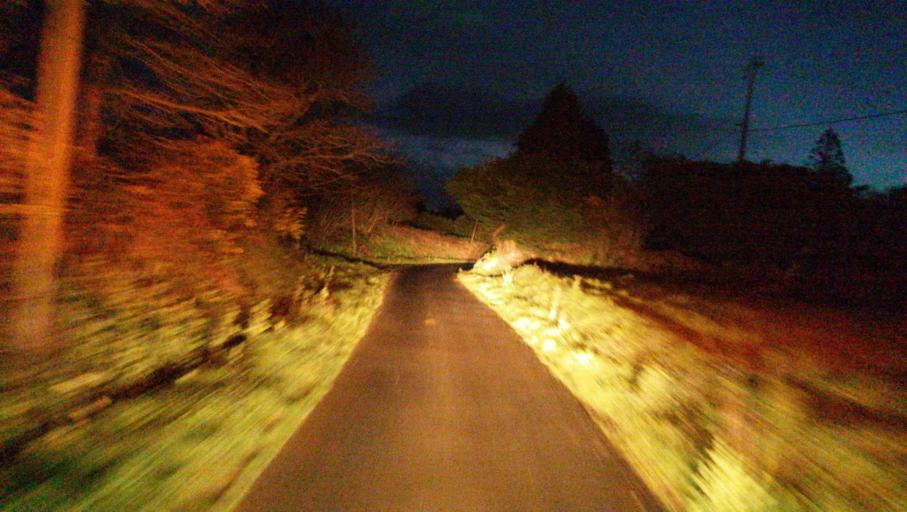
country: FR
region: Brittany
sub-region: Departement des Cotes-d'Armor
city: Plouha
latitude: 48.6764
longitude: -2.9451
